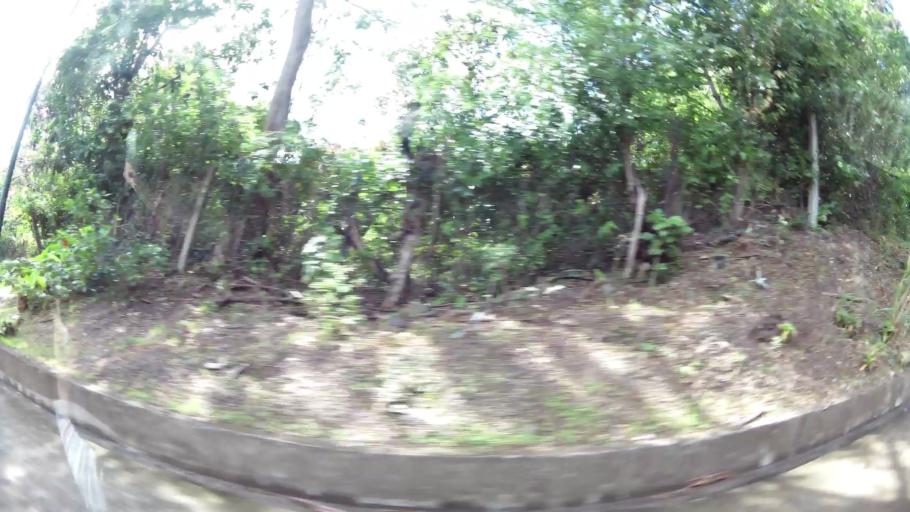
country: MQ
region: Martinique
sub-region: Martinique
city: Les Trois-Ilets
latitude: 14.4808
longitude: -61.0141
